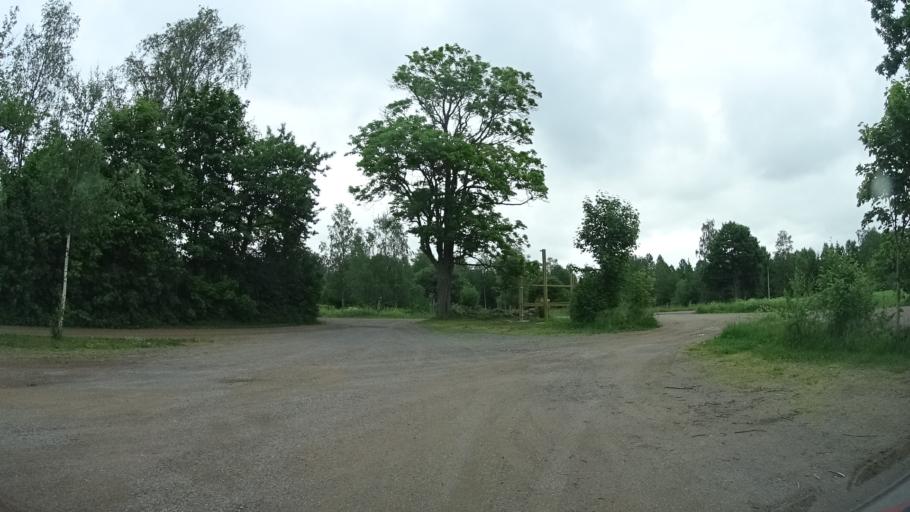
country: SE
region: Joenkoeping
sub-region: Eksjo Kommun
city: Mariannelund
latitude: 57.6904
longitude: 15.5580
